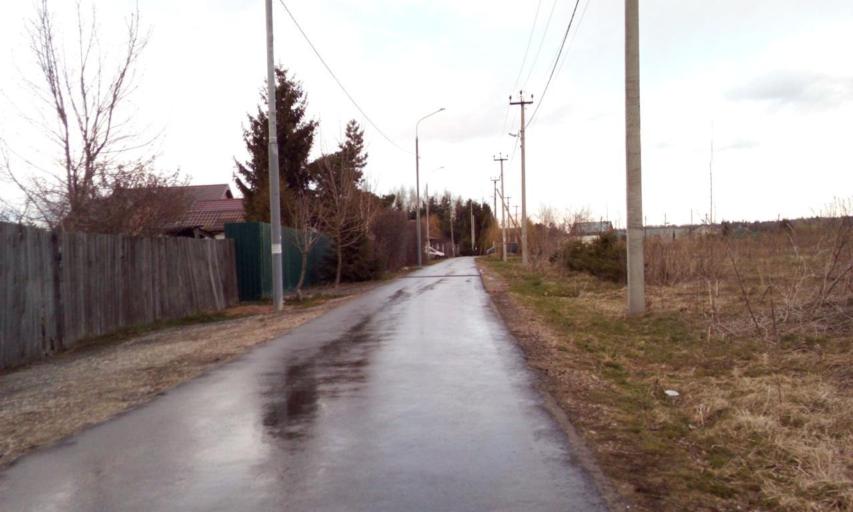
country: RU
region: Moskovskaya
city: Troitsk
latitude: 55.5216
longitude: 37.2653
